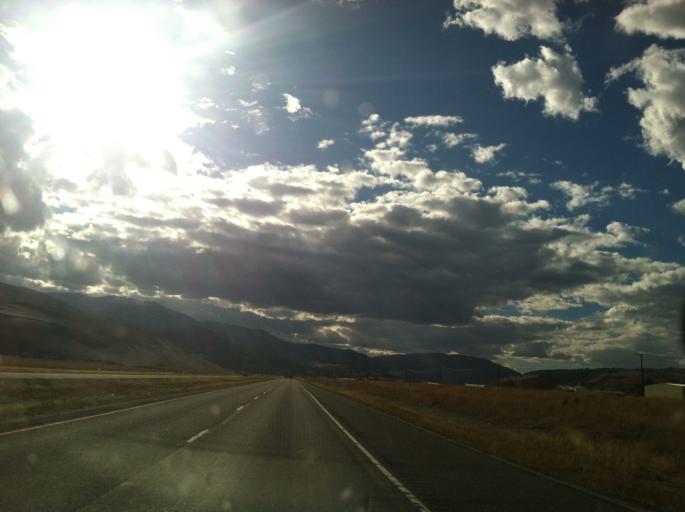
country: US
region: Montana
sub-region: Deer Lodge County
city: Anaconda
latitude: 46.1280
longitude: -112.9030
